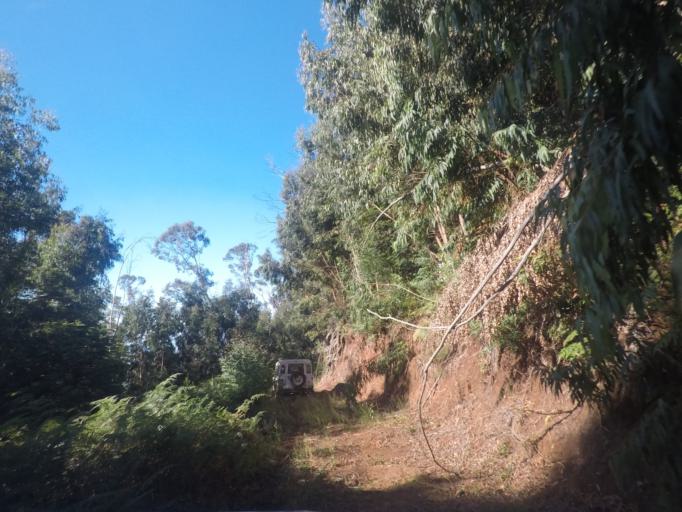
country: PT
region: Madeira
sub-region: Funchal
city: Nossa Senhora do Monte
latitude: 32.6917
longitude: -16.9113
